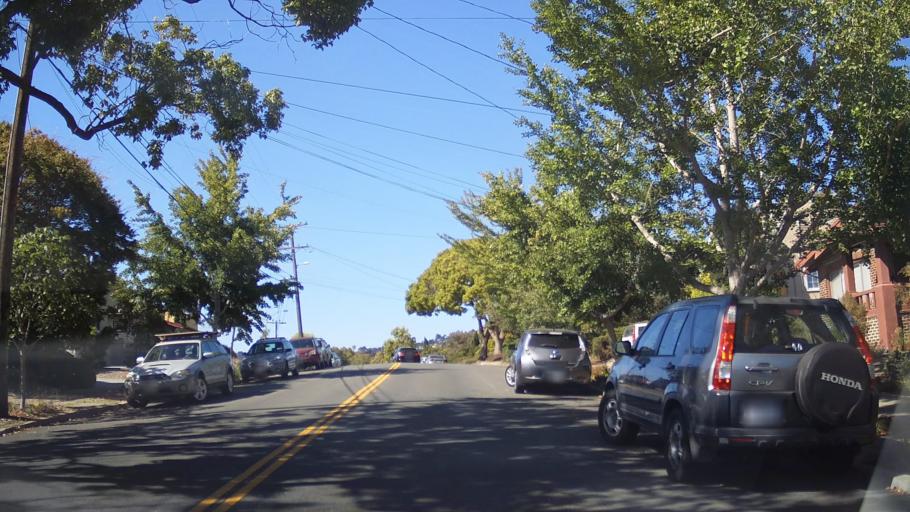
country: US
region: California
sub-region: Alameda County
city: Albany
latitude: 37.8879
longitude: -122.2851
